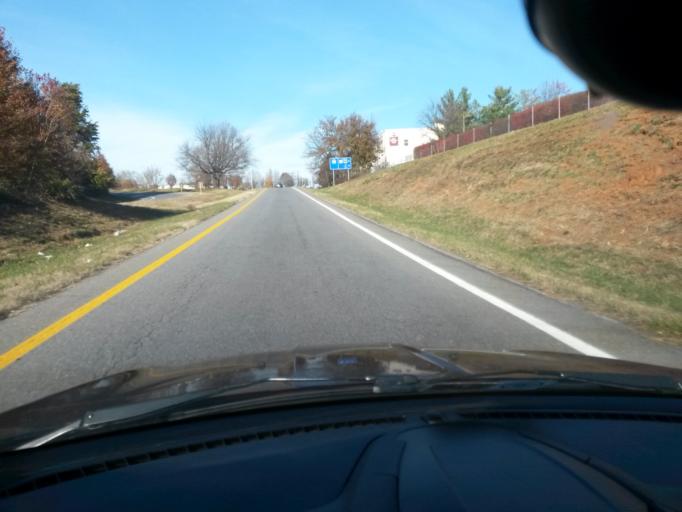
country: US
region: Virginia
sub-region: Roanoke County
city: Hollins
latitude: 37.3081
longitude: -79.9716
